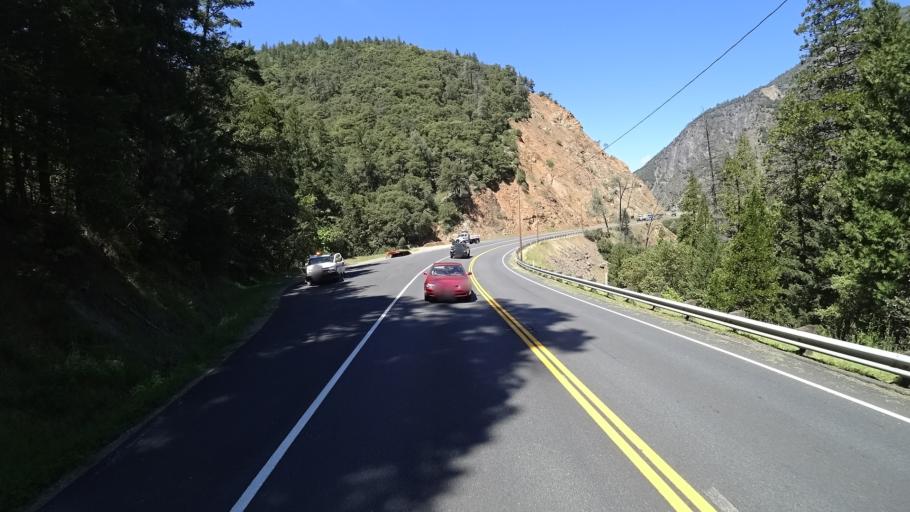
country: US
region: California
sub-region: Humboldt County
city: Willow Creek
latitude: 40.8125
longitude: -123.4787
